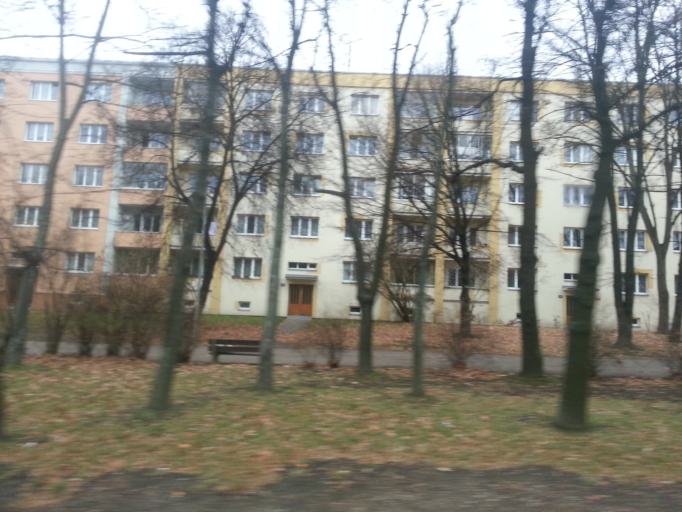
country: CZ
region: Central Bohemia
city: Horomerice
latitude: 50.0876
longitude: 14.3499
